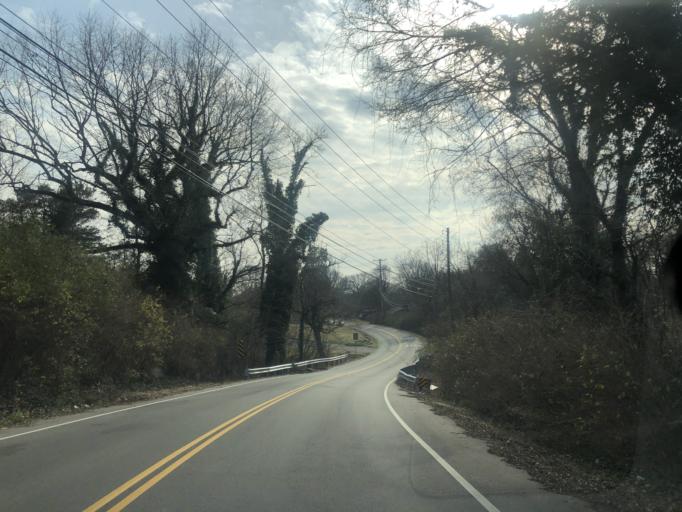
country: US
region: Tennessee
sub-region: Davidson County
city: Oak Hill
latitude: 36.1101
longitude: -86.7090
